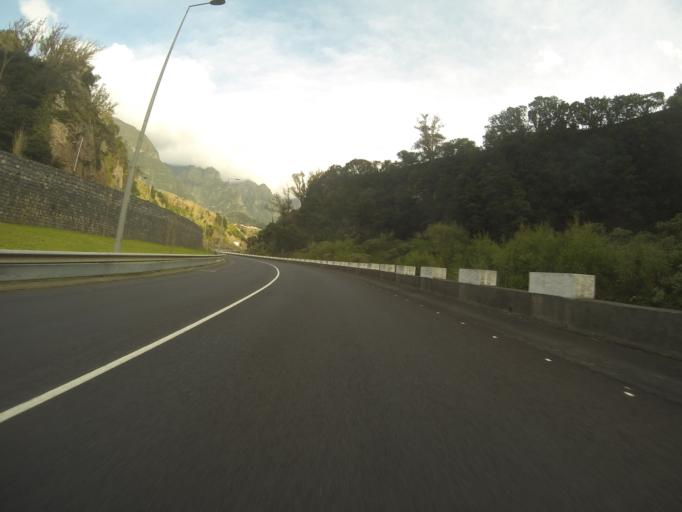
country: PT
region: Madeira
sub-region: Sao Vicente
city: Sao Vicente
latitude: 32.7946
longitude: -17.0396
